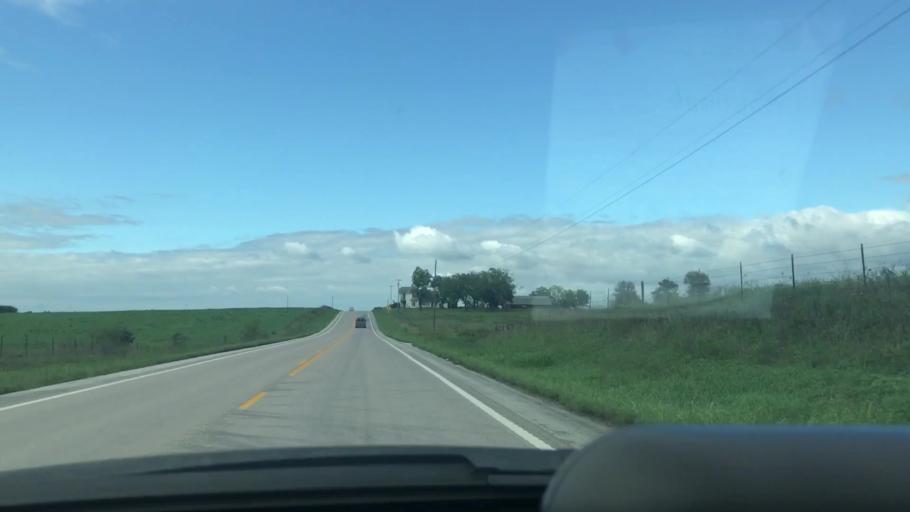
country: US
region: Missouri
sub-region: Hickory County
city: Hermitage
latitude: 37.9517
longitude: -93.2075
